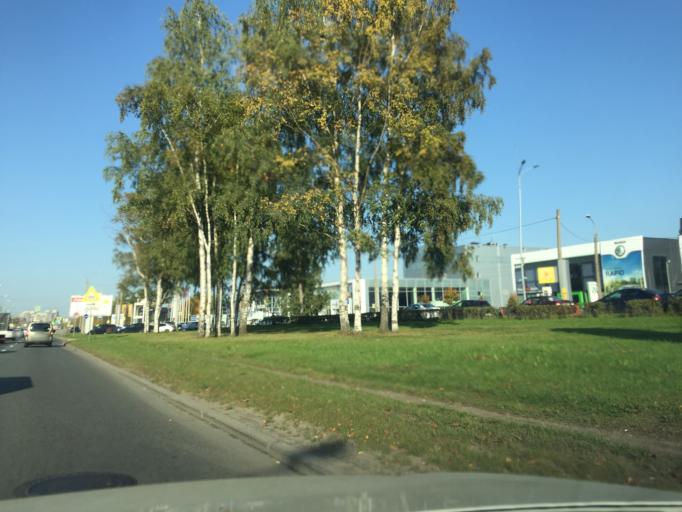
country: RU
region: Leningrad
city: Akademicheskoe
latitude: 60.0055
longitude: 30.4358
